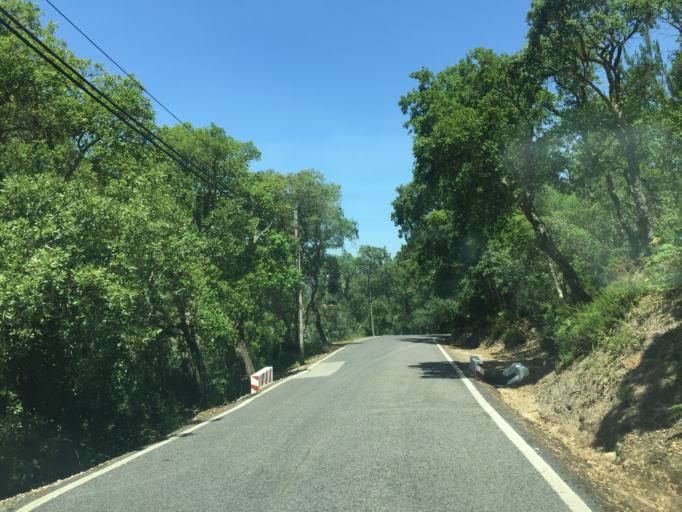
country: PT
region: Lisbon
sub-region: Mafra
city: Venda do Pinheiro
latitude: 38.8907
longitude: -9.2207
